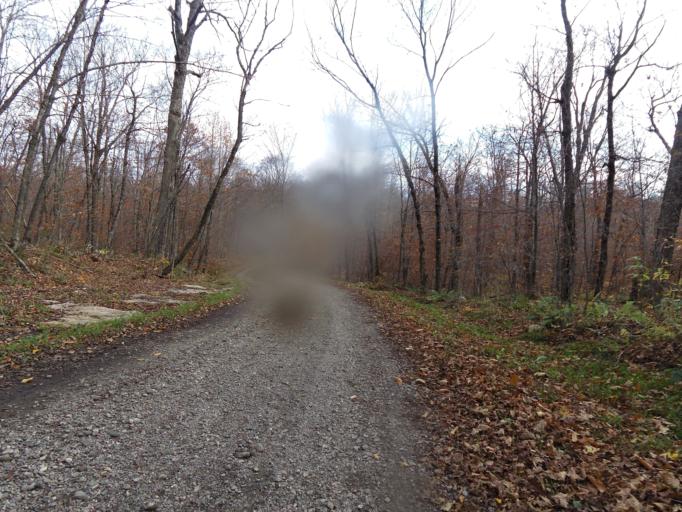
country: CA
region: Quebec
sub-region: Outaouais
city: Wakefield
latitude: 45.5531
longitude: -75.9715
